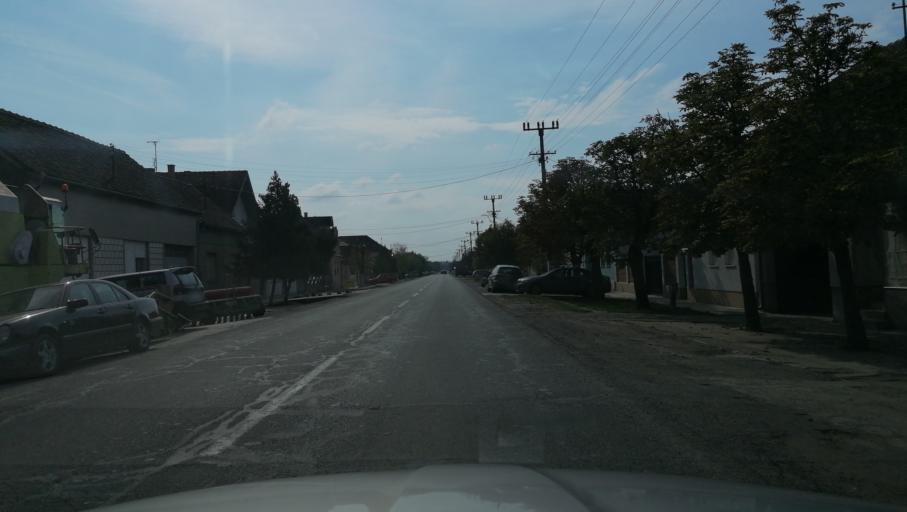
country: RS
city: Ravnje
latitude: 45.0212
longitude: 19.4024
